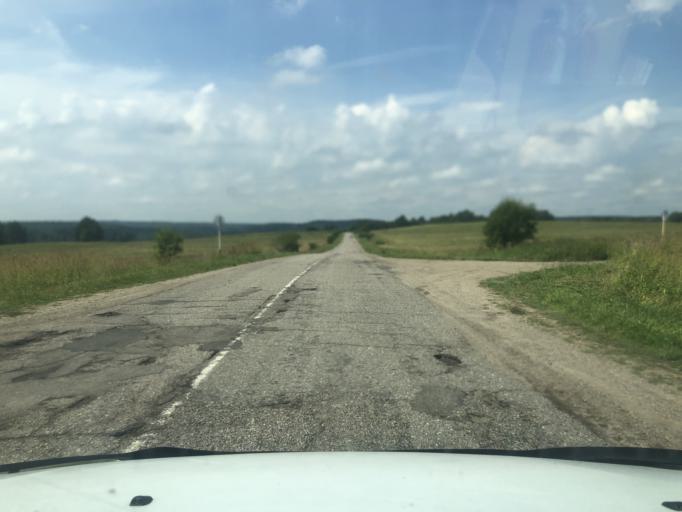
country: RU
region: Jaroslavl
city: Pereslavl'-Zalesskiy
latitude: 57.0385
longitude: 38.8880
